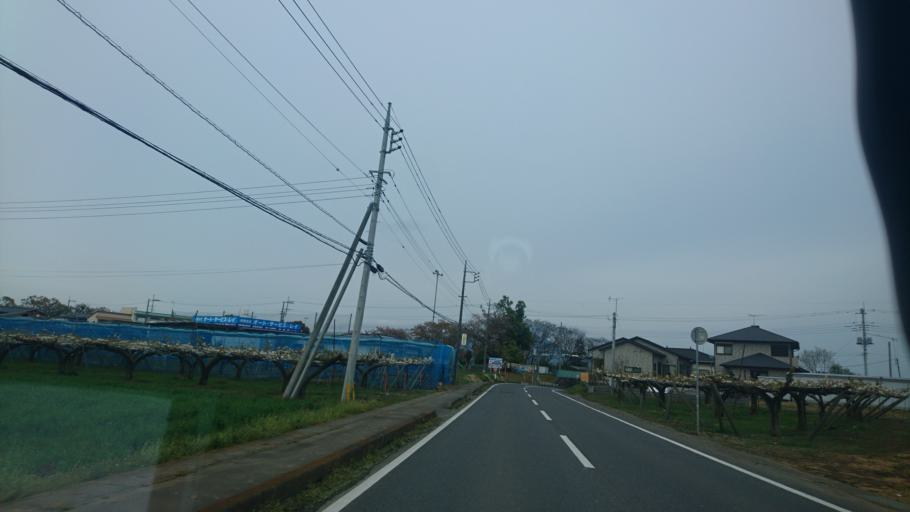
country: JP
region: Ibaraki
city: Shimodate
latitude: 36.2200
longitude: 139.9809
